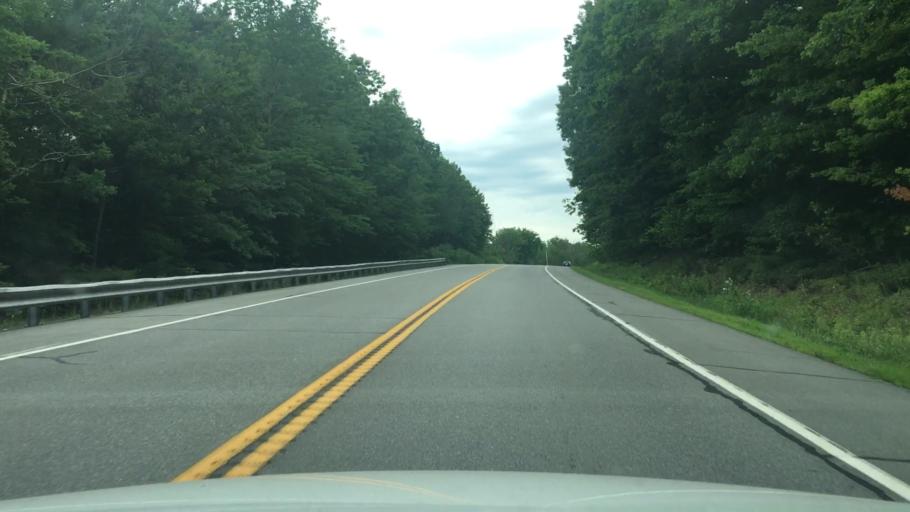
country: US
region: Maine
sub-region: Kennebec County
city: Windsor
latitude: 44.3669
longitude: -69.6329
